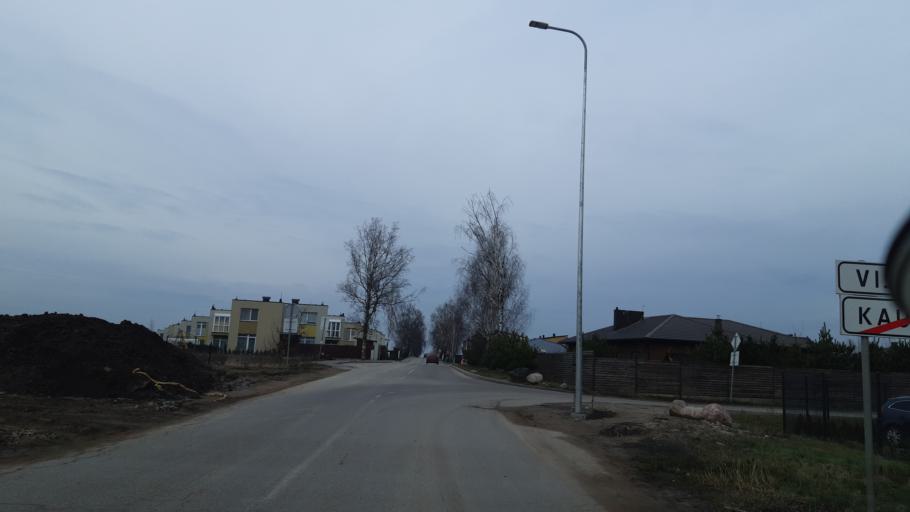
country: LT
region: Kauno apskritis
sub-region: Kauno rajonas
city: Akademija (Kaunas)
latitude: 54.9473
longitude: 23.8286
